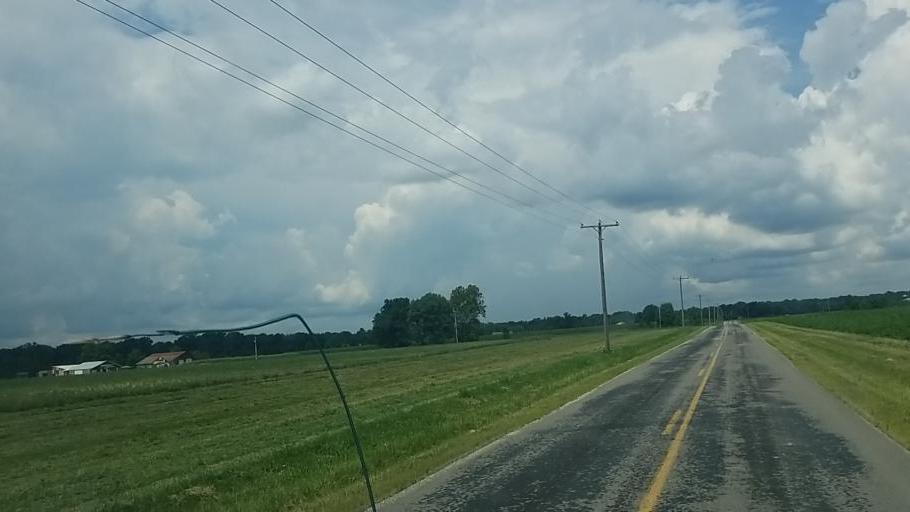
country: US
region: Ohio
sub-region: Medina County
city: Lodi
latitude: 41.1298
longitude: -82.0744
